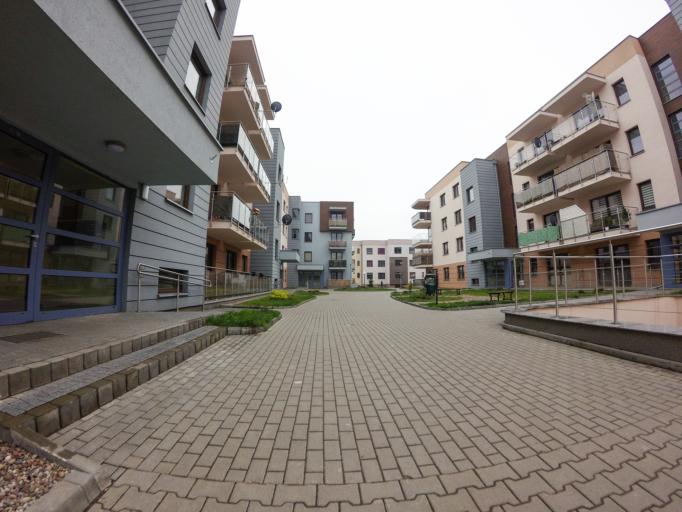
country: PL
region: Kujawsko-Pomorskie
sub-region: Powiat bydgoski
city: Osielsko
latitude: 53.1557
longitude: 18.1039
